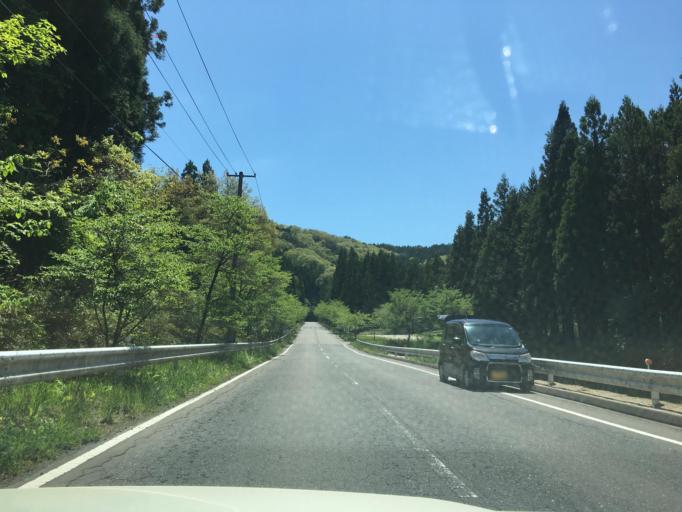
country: JP
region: Fukushima
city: Funehikimachi-funehiki
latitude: 37.3509
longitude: 140.6318
